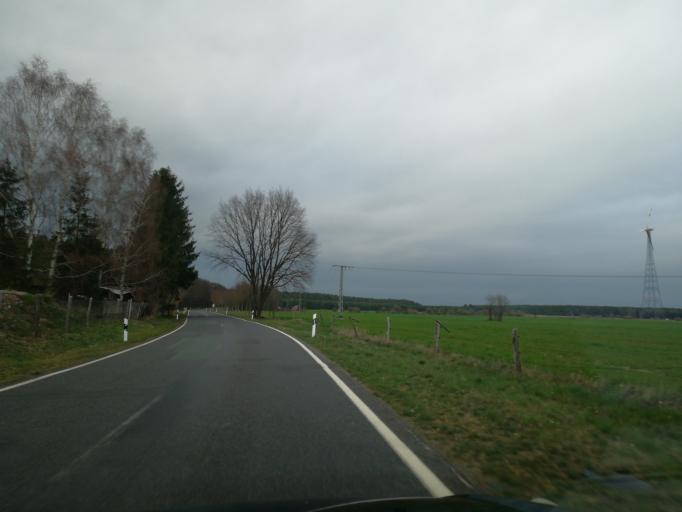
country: DE
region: Brandenburg
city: Vetschau
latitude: 51.7184
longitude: 14.0908
